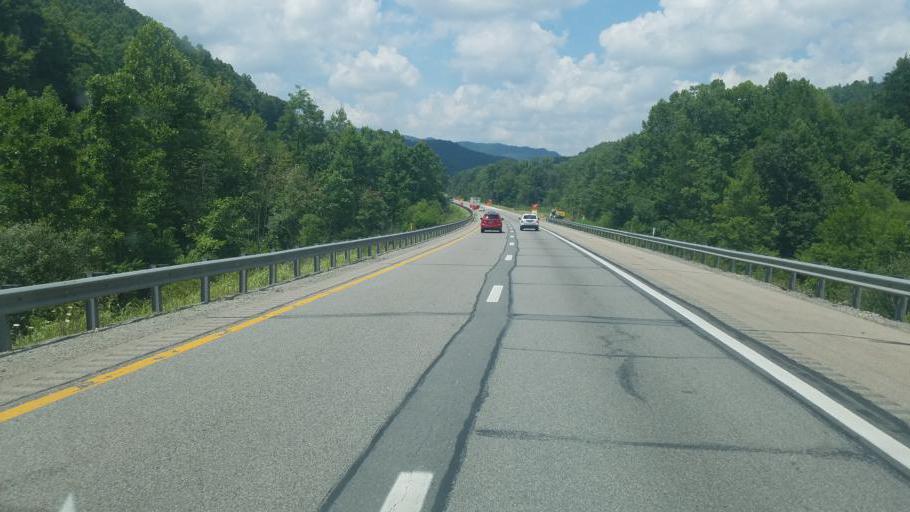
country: US
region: West Virginia
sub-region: Raleigh County
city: Prosperity
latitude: 37.8559
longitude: -81.2530
